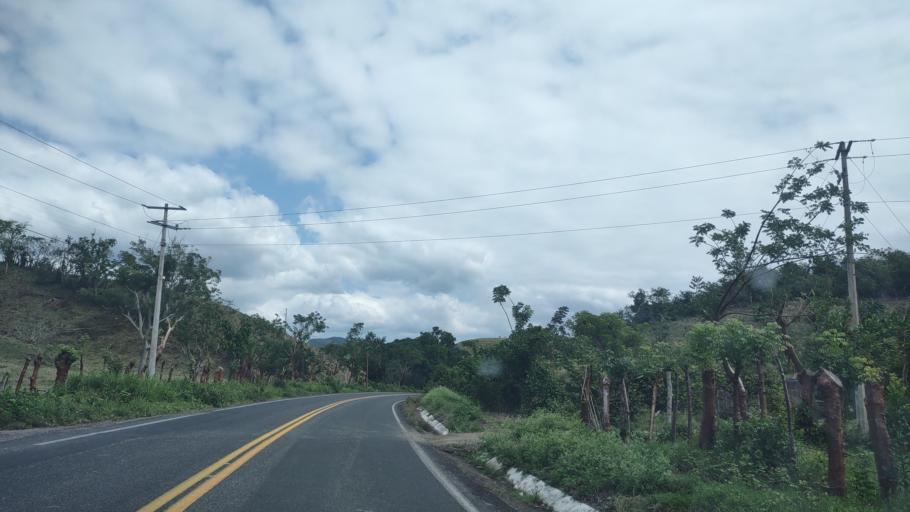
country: MX
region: Veracruz
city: Papantla de Olarte
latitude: 20.4637
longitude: -97.2753
